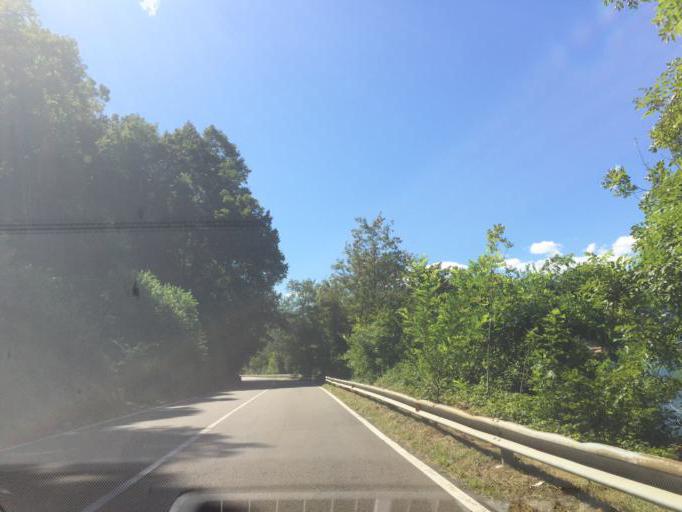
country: IT
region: Lombardy
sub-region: Provincia di Varese
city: Brusimpiano
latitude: 45.9546
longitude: 8.8861
